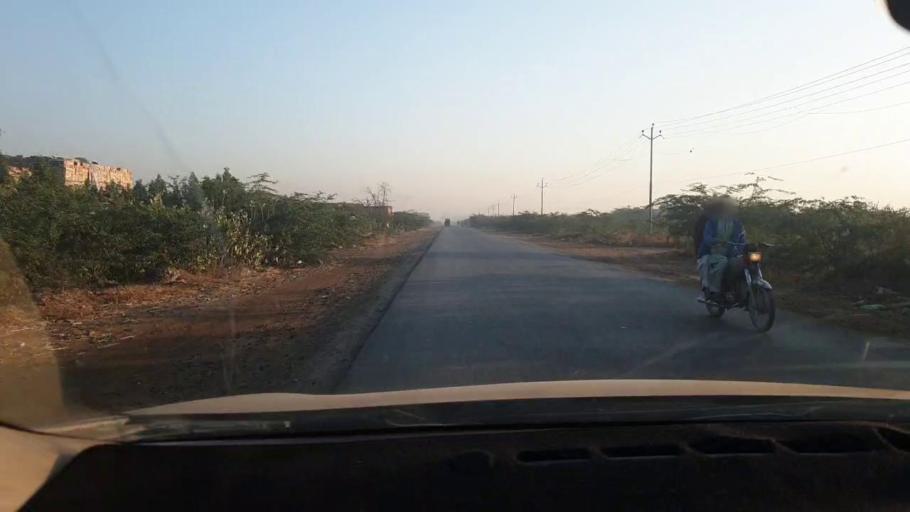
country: PK
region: Sindh
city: Malir Cantonment
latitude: 24.9982
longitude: 67.1447
